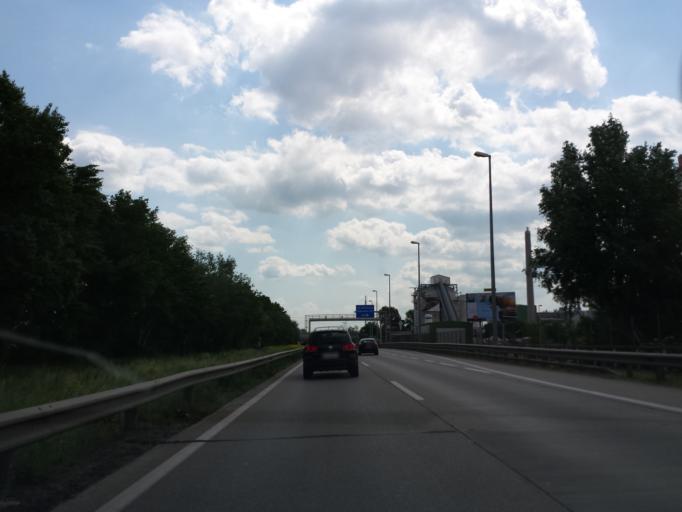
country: AT
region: Vienna
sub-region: Wien Stadt
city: Vienna
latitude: 48.1875
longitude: 16.4261
